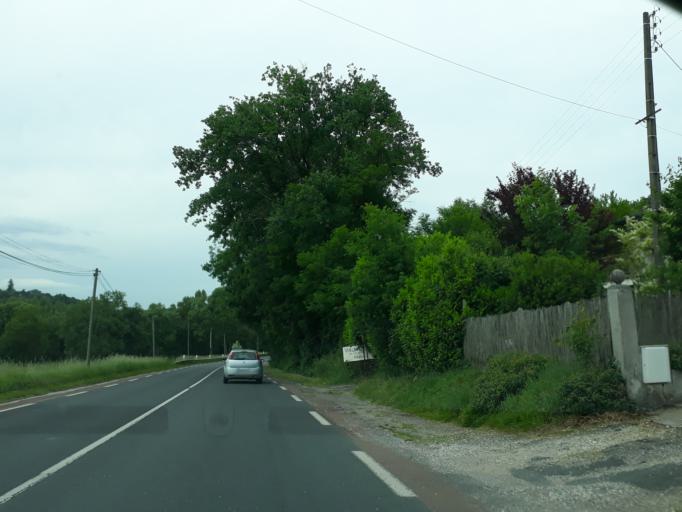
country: FR
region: Limousin
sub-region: Departement de la Correze
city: Saint-Pantaleon-de-Larche
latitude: 45.1324
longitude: 1.4446
